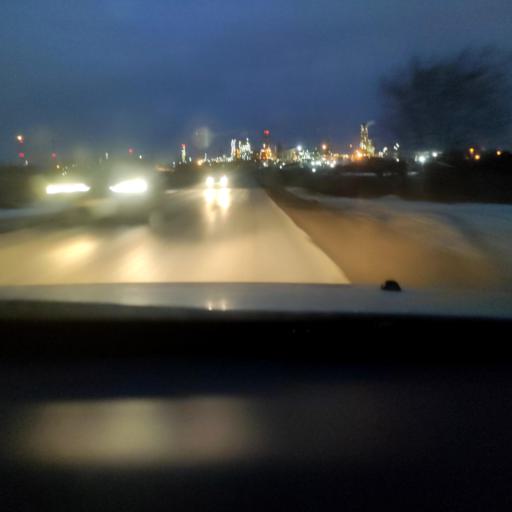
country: RU
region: Perm
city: Gamovo
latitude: 57.9009
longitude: 56.1201
